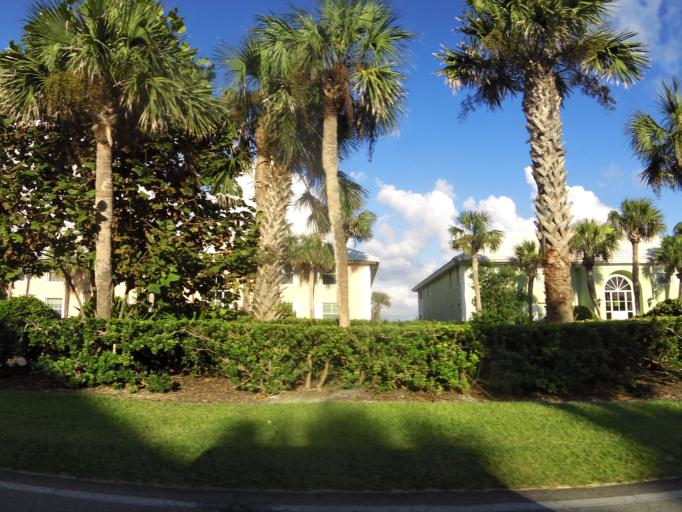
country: US
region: Florida
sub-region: Saint Johns County
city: Sawgrass
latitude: 30.2149
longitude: -81.3711
